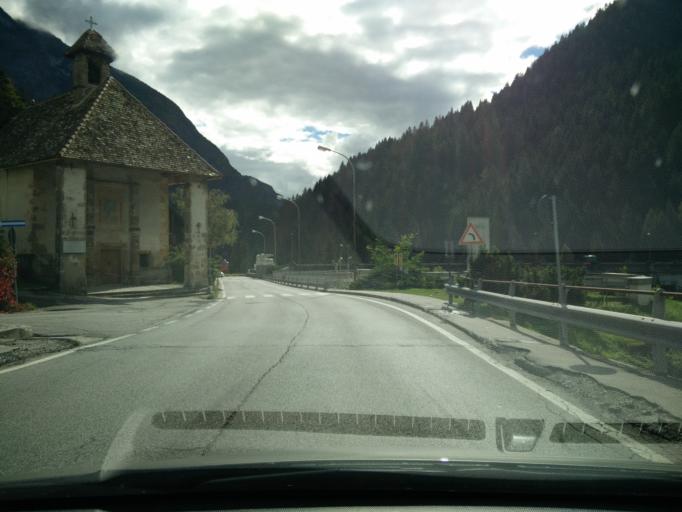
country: IT
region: Veneto
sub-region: Provincia di Belluno
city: Vigo di Cadore
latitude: 46.5401
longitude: 12.4631
